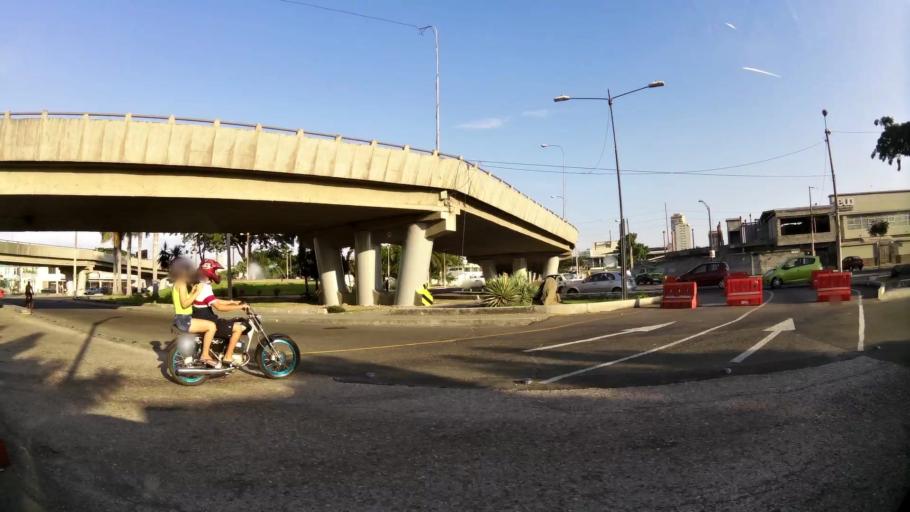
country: EC
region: Guayas
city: Guayaquil
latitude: -2.1813
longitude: -79.8927
